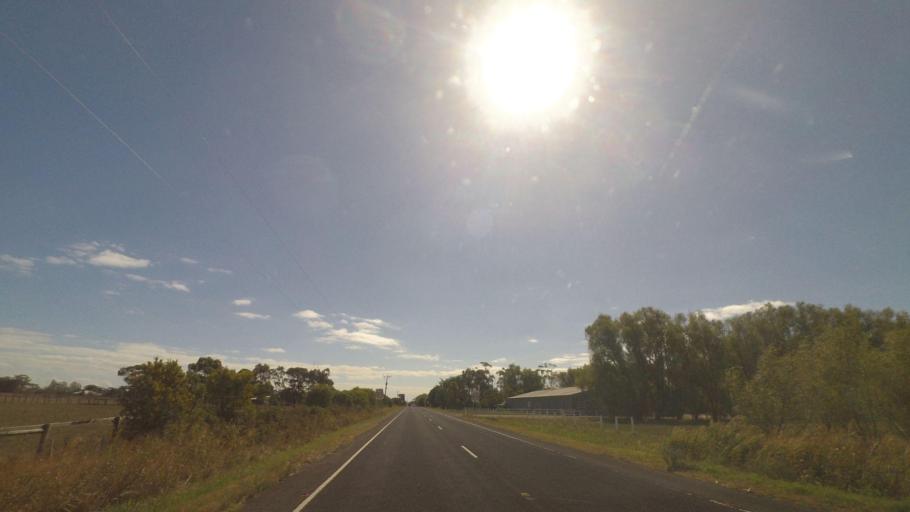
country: AU
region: Victoria
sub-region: Cardinia
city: Pakenham South
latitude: -38.1569
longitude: 145.5098
